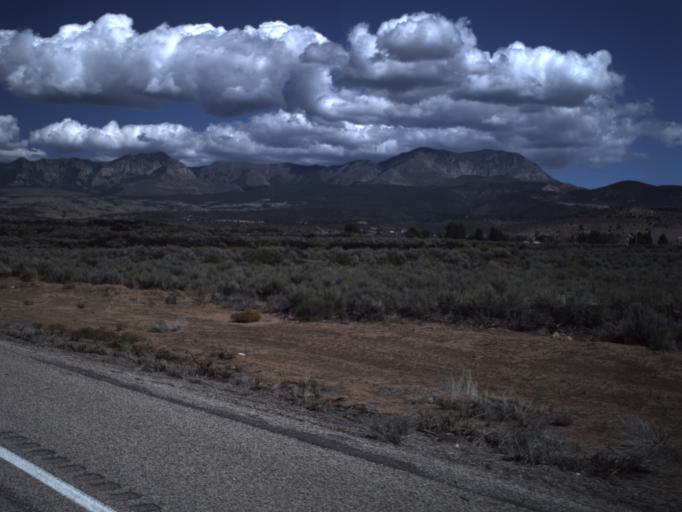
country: US
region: Utah
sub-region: Washington County
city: Ivins
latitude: 37.2482
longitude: -113.6270
